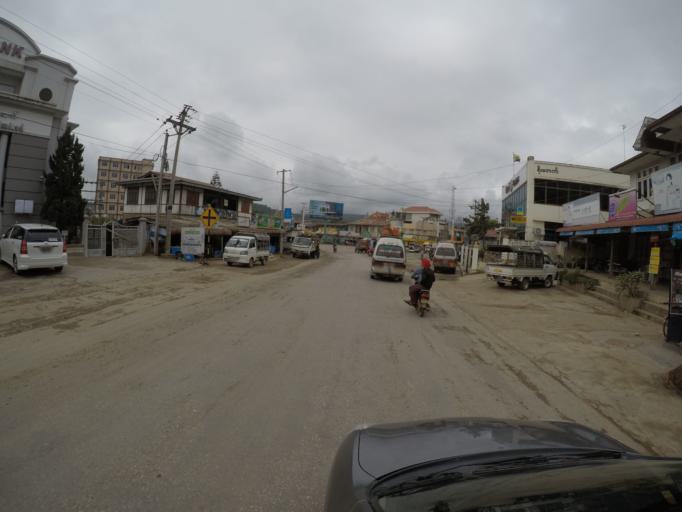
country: MM
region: Shan
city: Taunggyi
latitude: 20.6587
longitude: 96.6338
